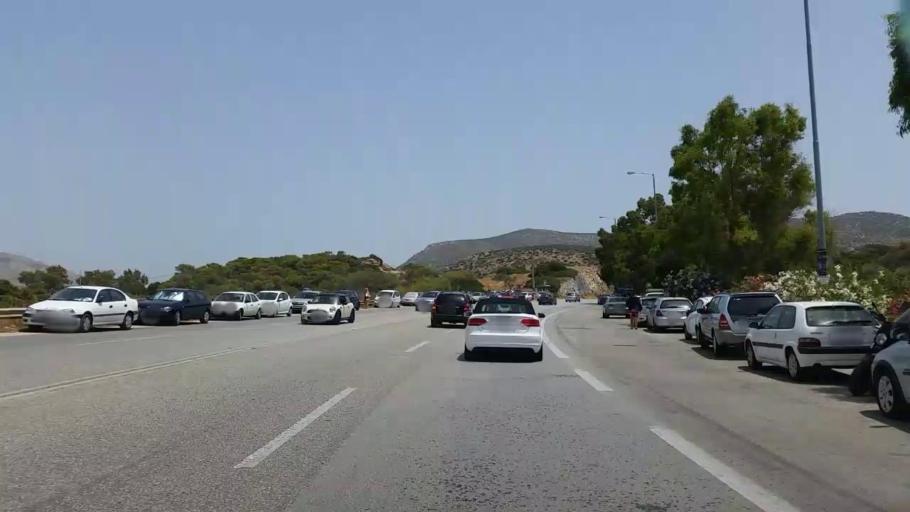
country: GR
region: Attica
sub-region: Nomarchia Anatolikis Attikis
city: Saronida
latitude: 37.7784
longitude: 23.8966
